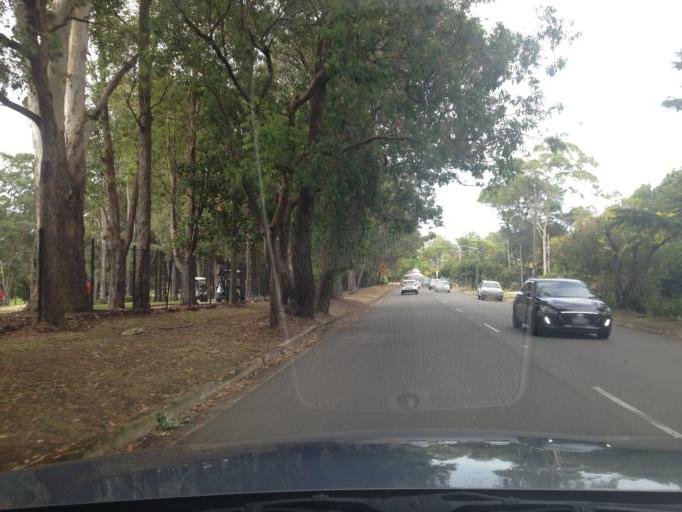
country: AU
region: New South Wales
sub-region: Ku-ring-gai
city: Killara
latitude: -33.7725
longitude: 151.1545
